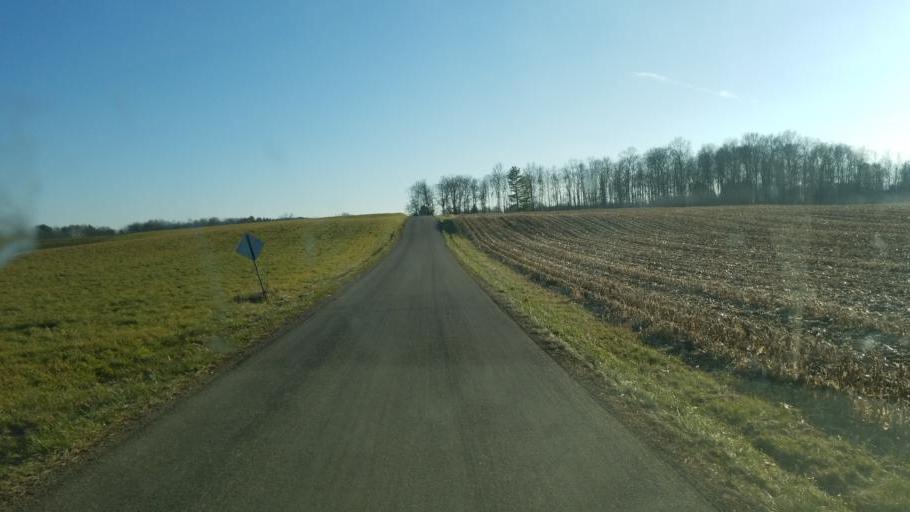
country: US
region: Ohio
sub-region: Richland County
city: Lexington
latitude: 40.6195
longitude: -82.6137
